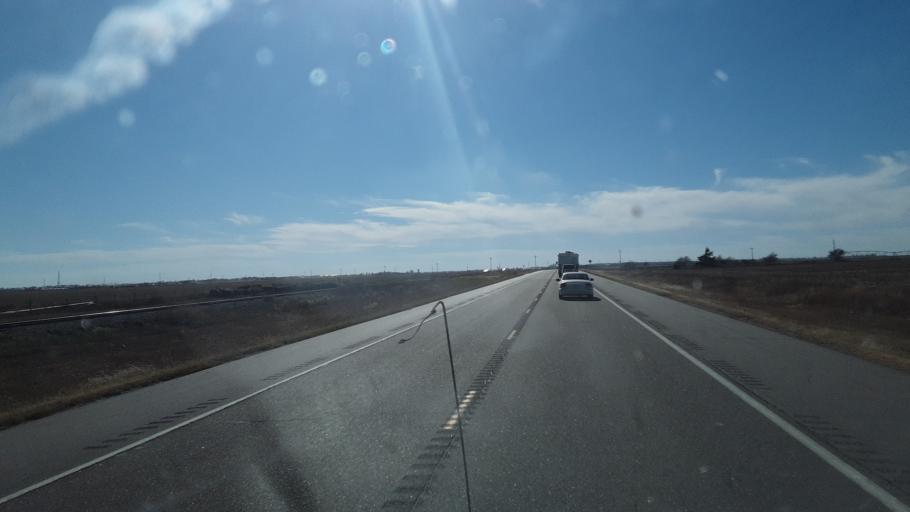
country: US
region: Kansas
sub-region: Pawnee County
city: Larned
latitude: 38.2267
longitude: -99.0370
